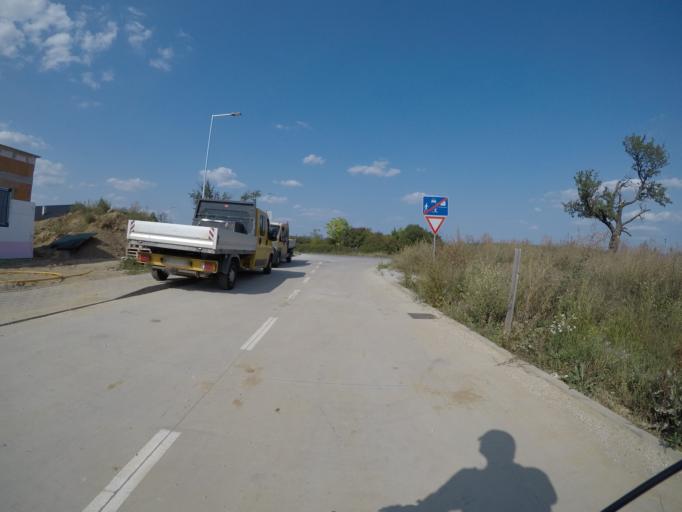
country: SK
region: Trenciansky
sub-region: Okres Nove Mesto nad Vahom
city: Nove Mesto nad Vahom
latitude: 48.7683
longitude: 17.8192
